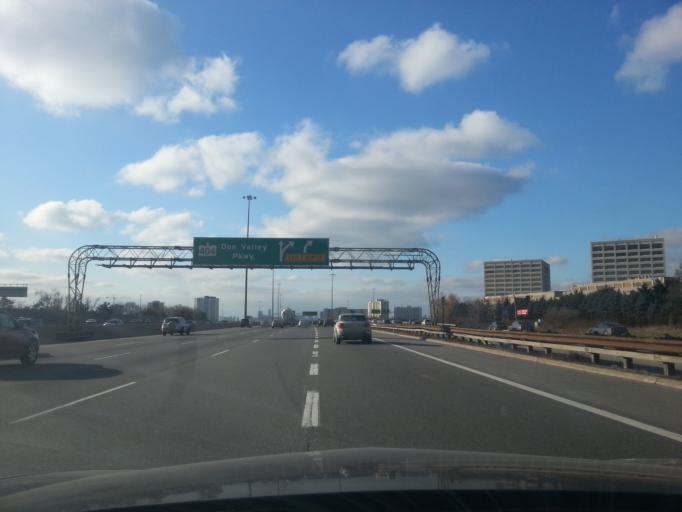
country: CA
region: Ontario
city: Scarborough
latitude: 43.7684
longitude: -79.3262
